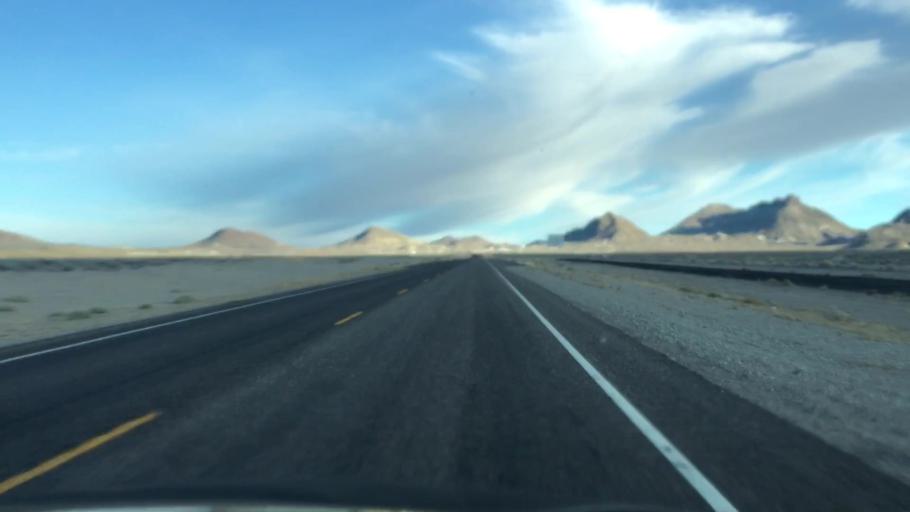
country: US
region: Nevada
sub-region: Nye County
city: Tonopah
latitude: 38.0870
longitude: -117.2871
